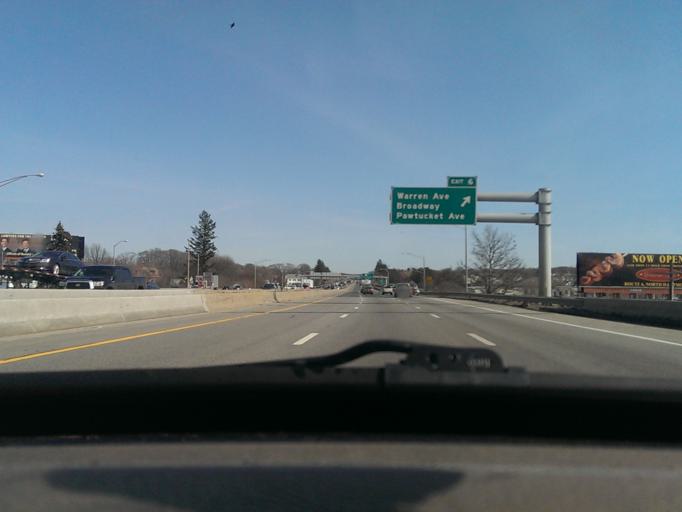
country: US
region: Rhode Island
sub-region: Providence County
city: East Providence
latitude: 41.8147
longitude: -71.3703
